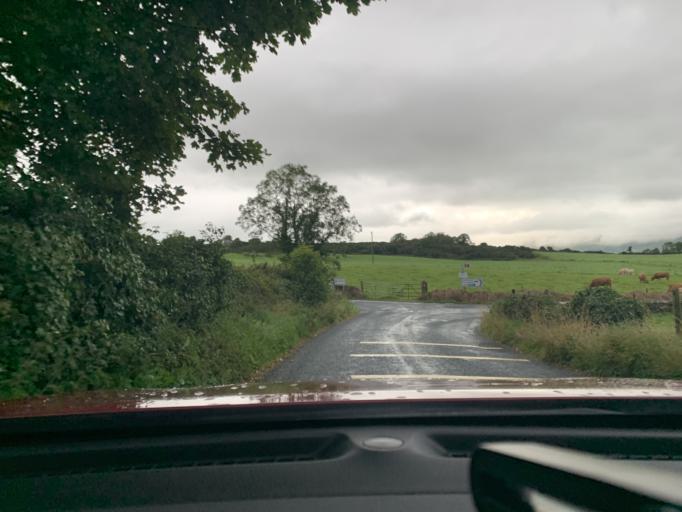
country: IE
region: Connaught
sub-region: Sligo
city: Sligo
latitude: 54.3066
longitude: -8.5139
